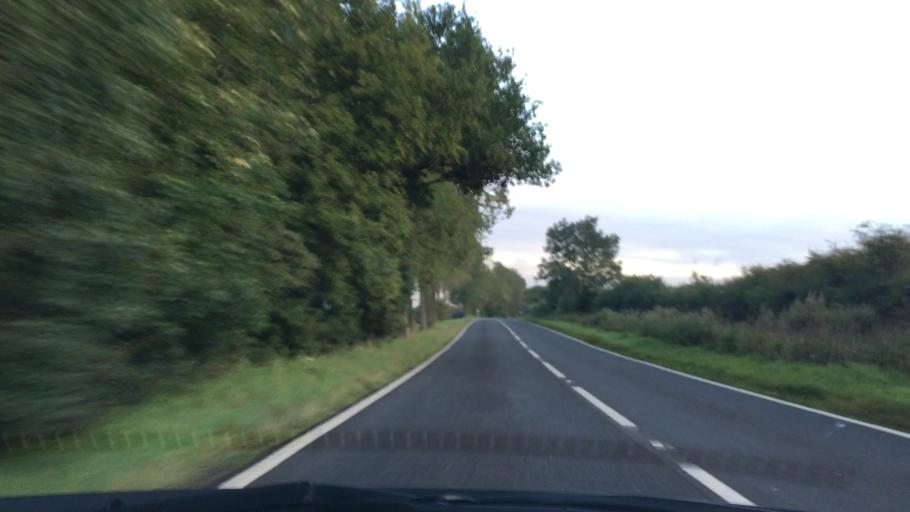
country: GB
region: England
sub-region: North East Lincolnshire
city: Wold Newton
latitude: 53.4725
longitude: -0.1110
